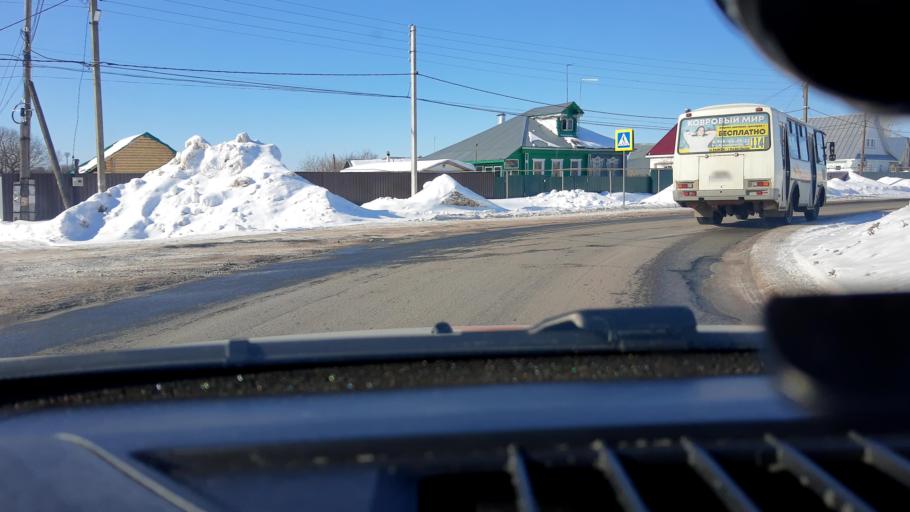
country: RU
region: Nizjnij Novgorod
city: Volodarsk
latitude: 56.2303
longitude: 43.1991
